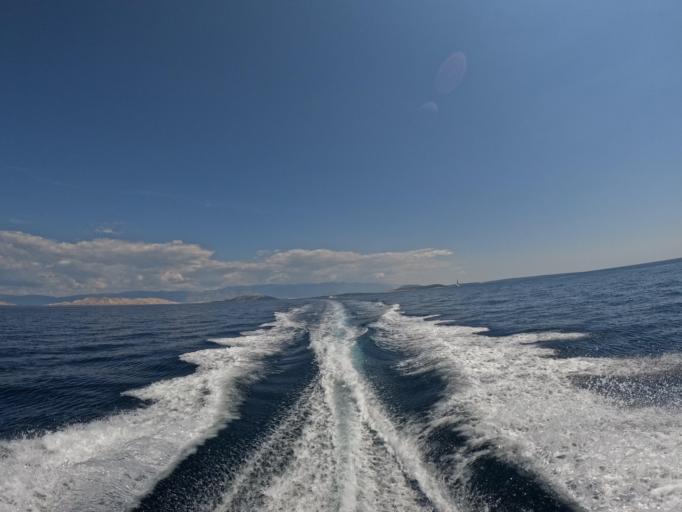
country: HR
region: Primorsko-Goranska
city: Punat
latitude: 44.8952
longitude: 14.6223
